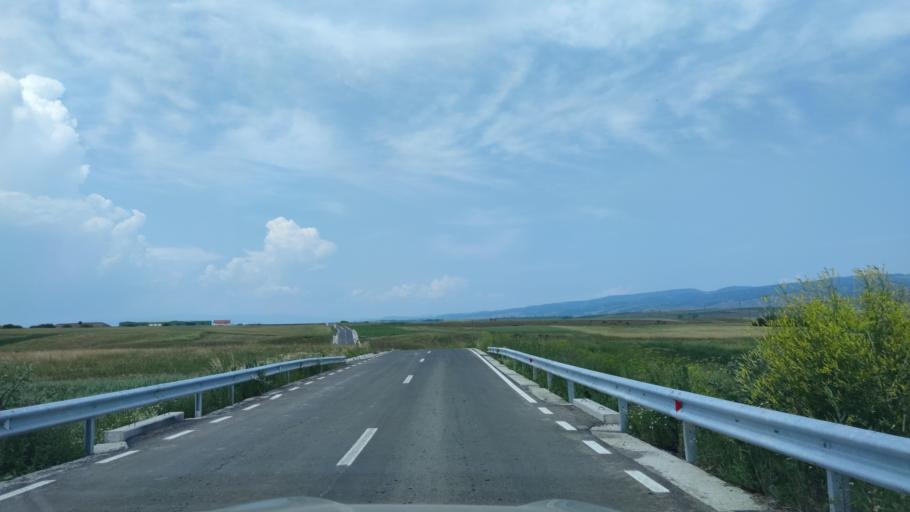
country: RO
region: Harghita
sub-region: Comuna Subcetate
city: Subcetate
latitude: 46.8194
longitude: 25.4476
